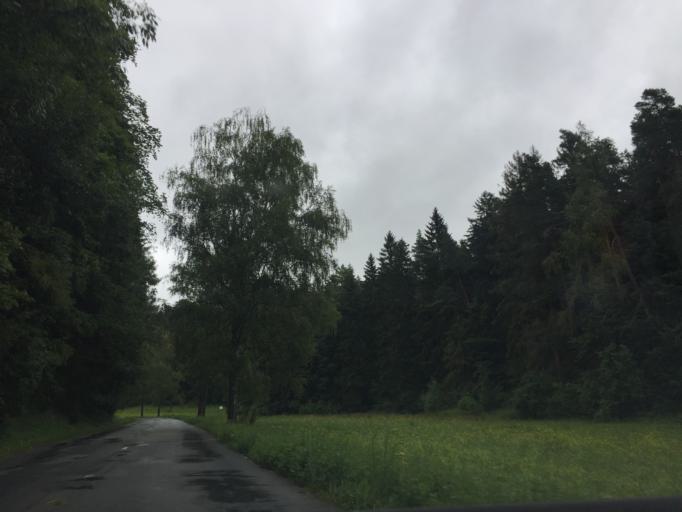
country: CZ
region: South Moravian
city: Ostrov u Macochy
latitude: 49.3860
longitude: 16.7669
